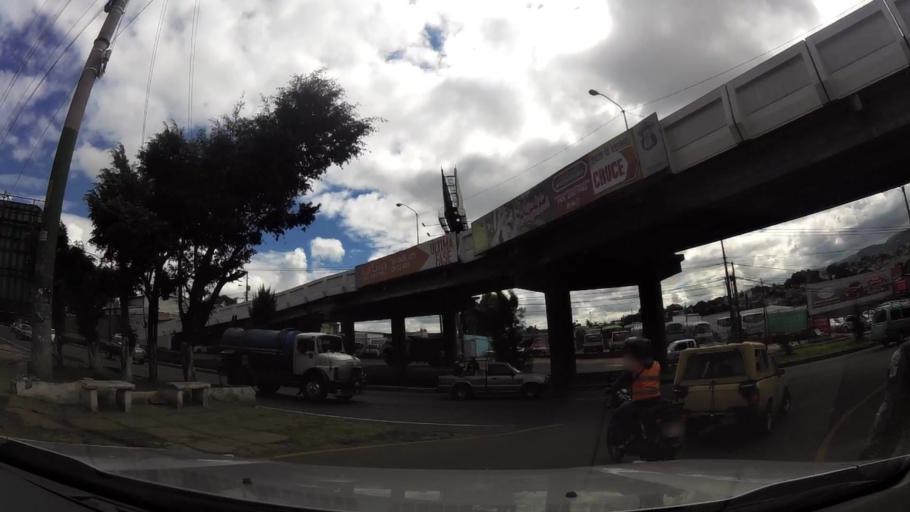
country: GT
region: Guatemala
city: Mixco
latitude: 14.6353
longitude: -90.5978
